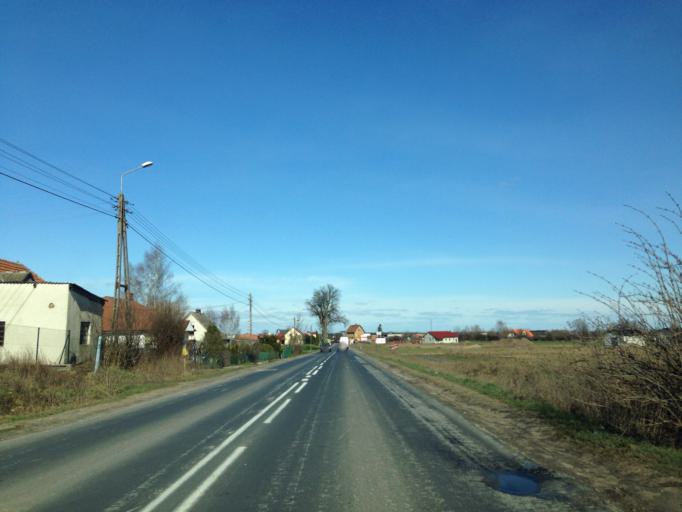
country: PL
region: Pomeranian Voivodeship
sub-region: Powiat malborski
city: Malbork
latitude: 54.0173
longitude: 19.0588
